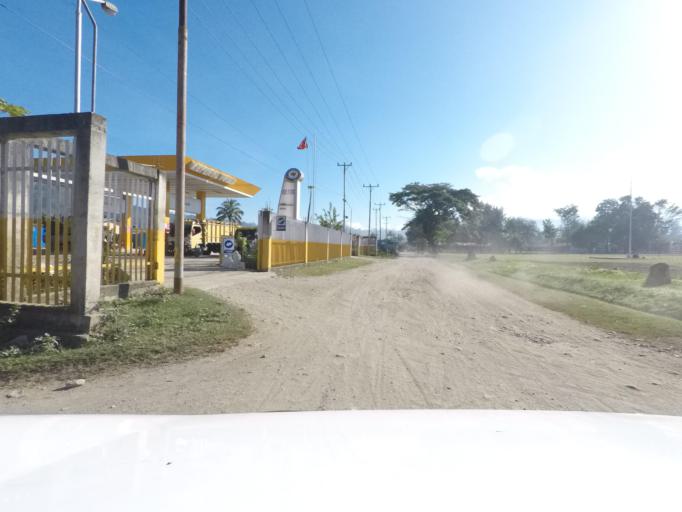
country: TL
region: Ermera
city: Gleno
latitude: -8.7239
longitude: 125.4313
